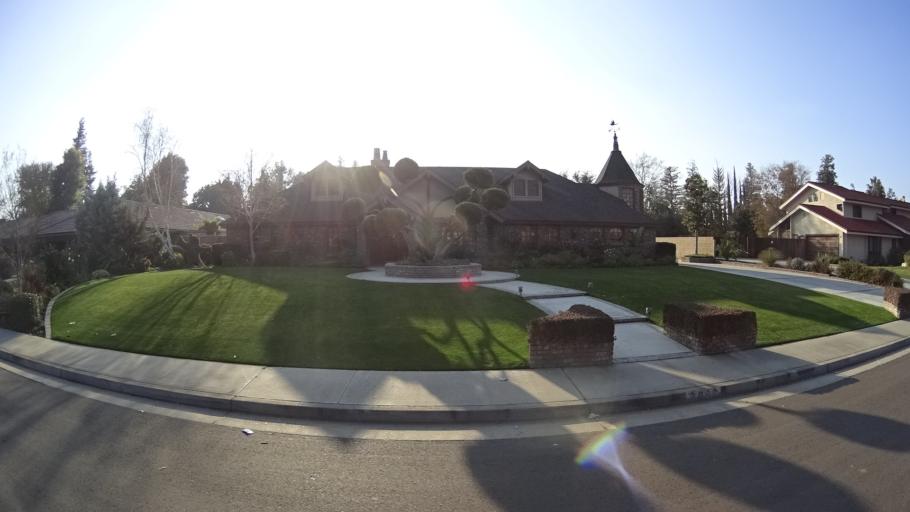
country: US
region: California
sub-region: Kern County
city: Greenacres
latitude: 35.3364
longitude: -119.1006
